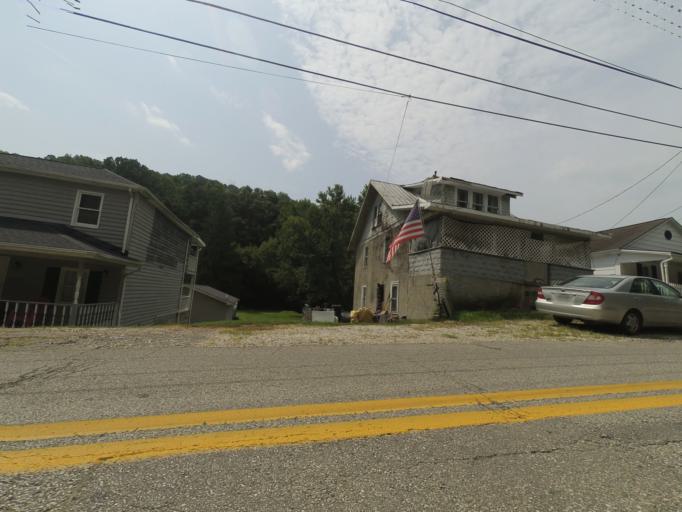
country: US
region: West Virginia
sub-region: Cabell County
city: Huntington
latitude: 38.3997
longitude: -82.4658
